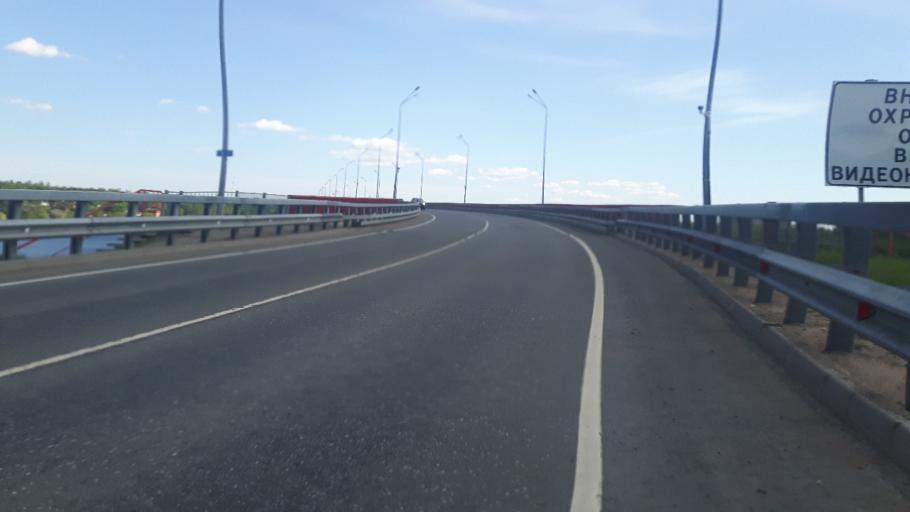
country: RU
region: Leningrad
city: Vyborg
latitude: 60.7389
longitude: 28.6849
